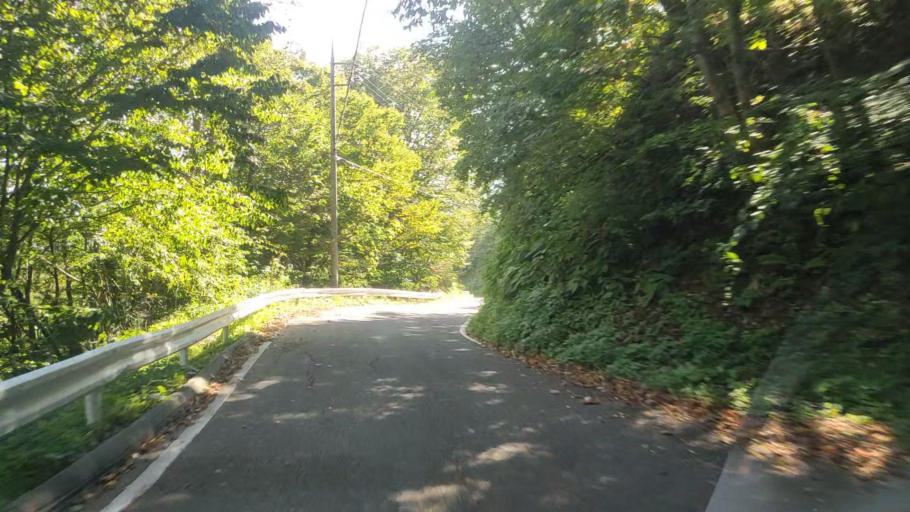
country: JP
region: Gunma
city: Nakanojomachi
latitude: 36.5974
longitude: 138.6840
